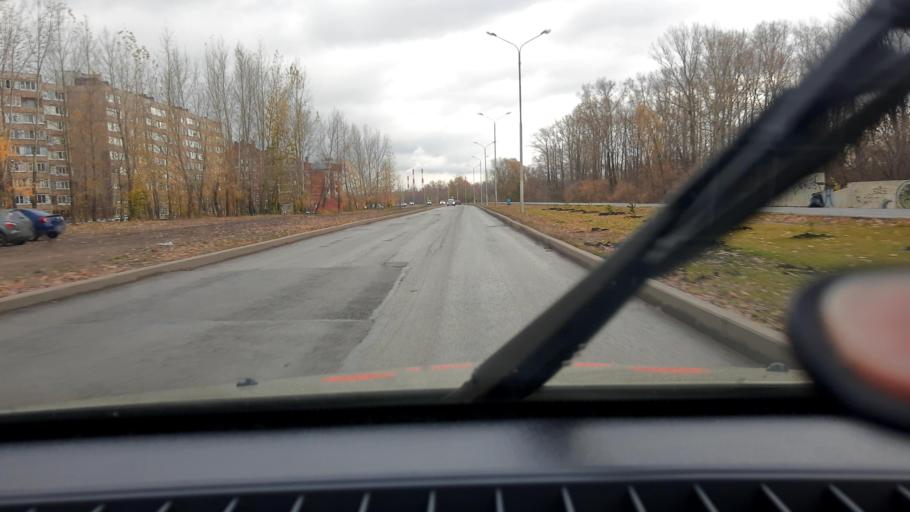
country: RU
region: Bashkortostan
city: Ufa
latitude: 54.7648
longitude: 56.0780
